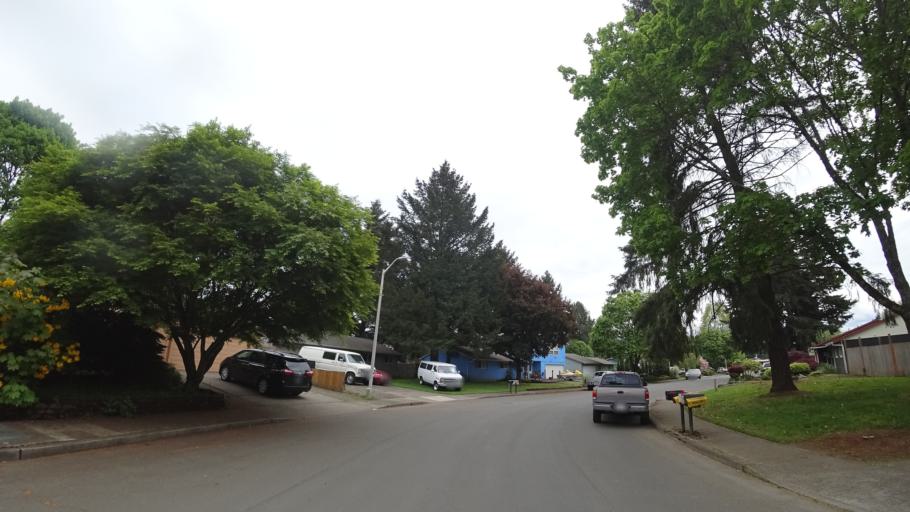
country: US
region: Oregon
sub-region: Washington County
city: Hillsboro
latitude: 45.5177
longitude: -122.9420
